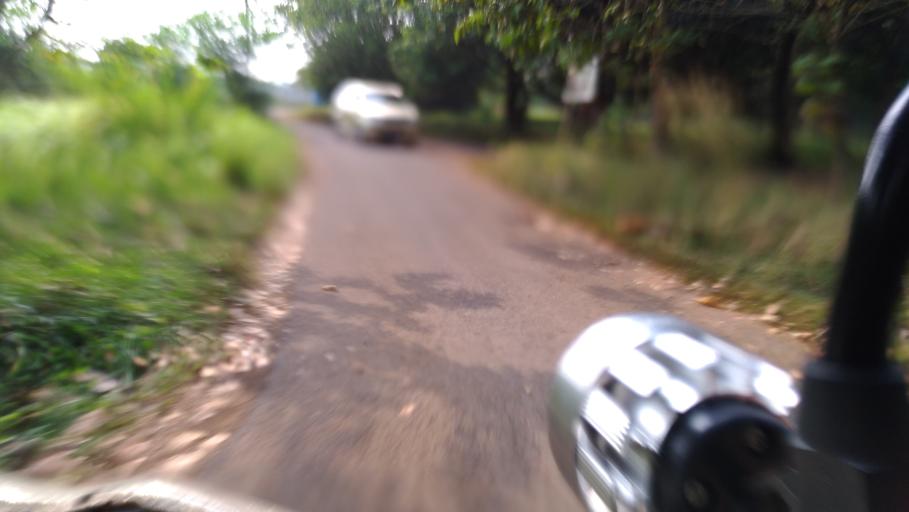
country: ID
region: West Java
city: Cileungsir
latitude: -6.3570
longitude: 106.8998
